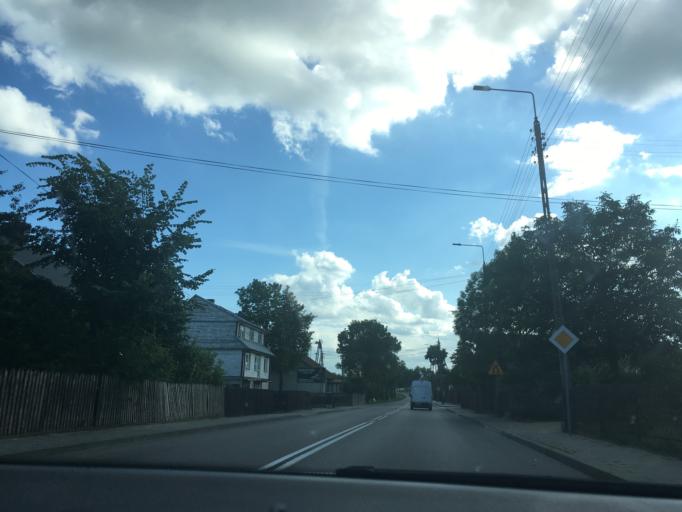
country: PL
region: Podlasie
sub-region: Powiat bialostocki
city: Zabludow
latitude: 53.0117
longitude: 23.3361
